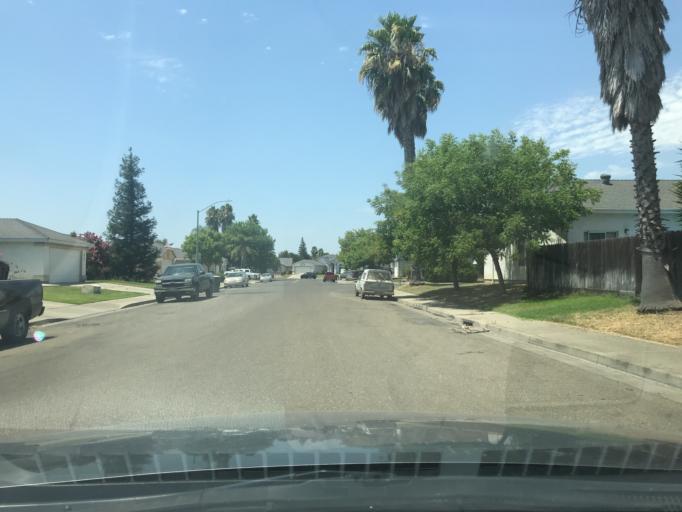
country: US
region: California
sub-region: Merced County
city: Atwater
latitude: 37.3627
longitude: -120.6001
